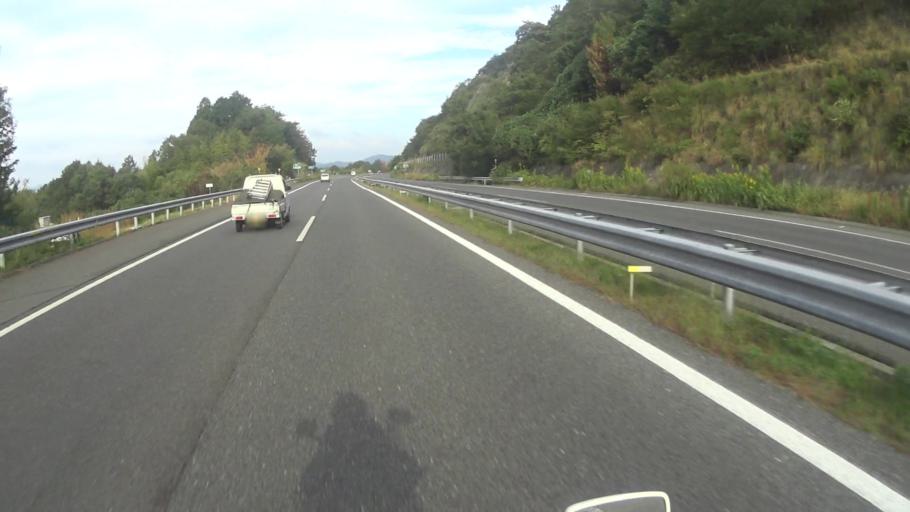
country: JP
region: Kyoto
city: Kameoka
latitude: 35.1019
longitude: 135.4920
